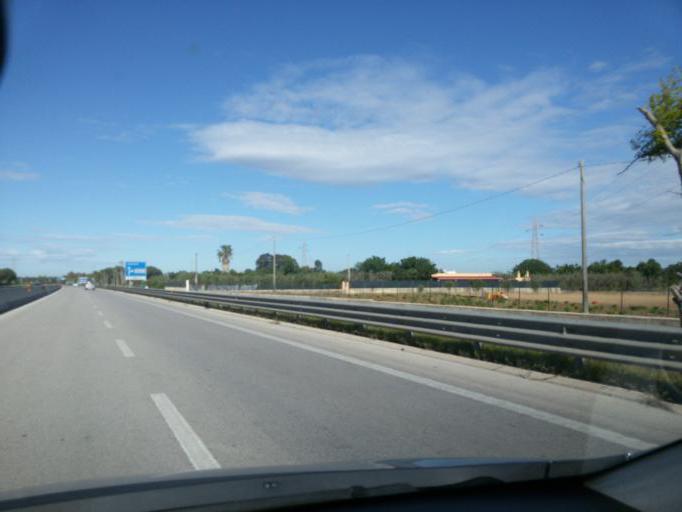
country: IT
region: Apulia
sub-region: Provincia di Brindisi
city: Oria
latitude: 40.5332
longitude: 17.6298
